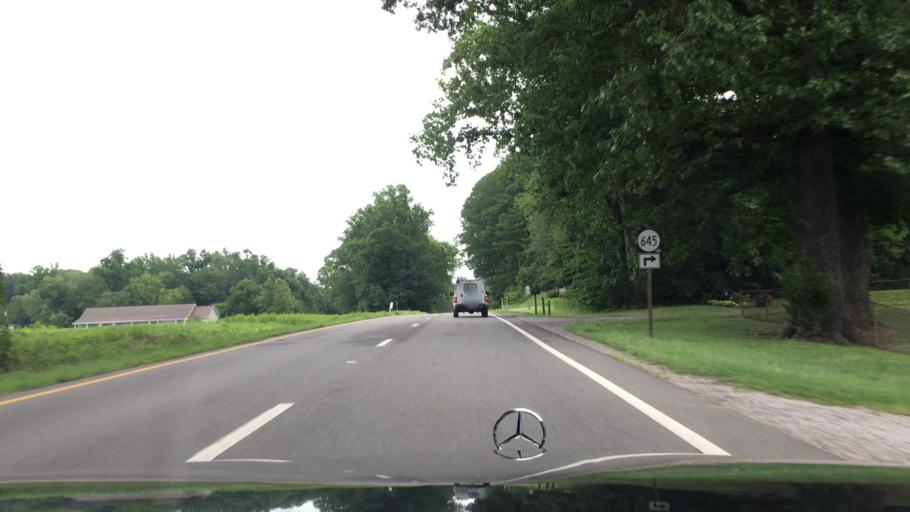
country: US
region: Virginia
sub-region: Prince Edward County
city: Hampden Sydney
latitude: 37.3110
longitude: -78.4980
